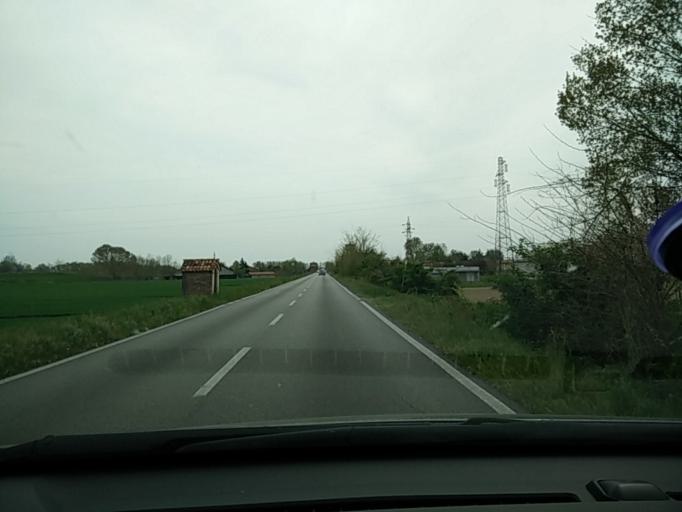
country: IT
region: Veneto
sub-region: Provincia di Venezia
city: Fossalta di Piave
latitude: 45.6384
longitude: 12.5216
